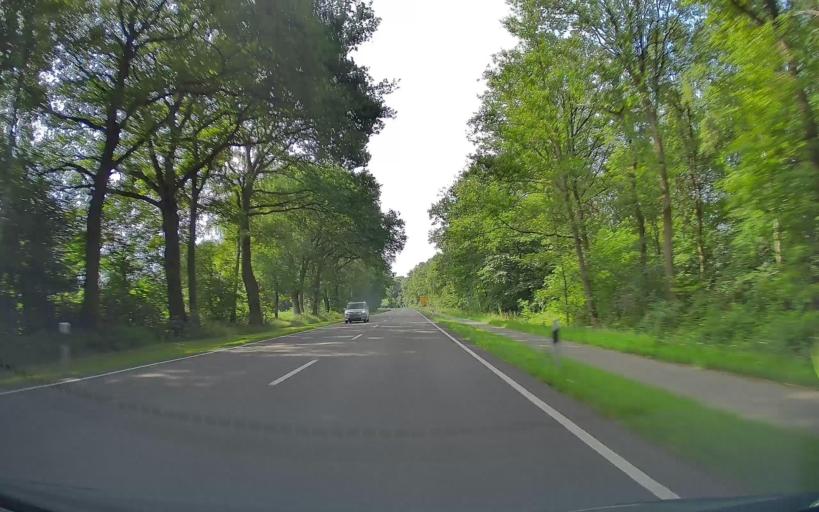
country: DE
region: Lower Saxony
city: Molbergen
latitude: 52.9216
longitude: 7.9531
